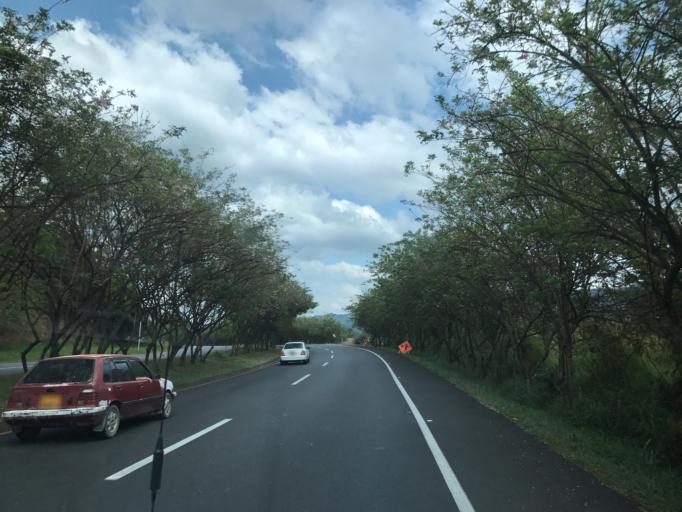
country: CO
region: Valle del Cauca
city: Obando
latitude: 4.6186
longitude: -75.9434
